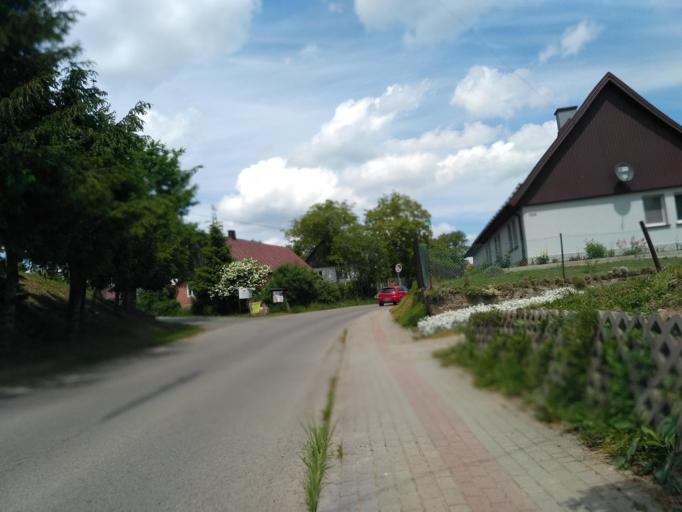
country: PL
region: Subcarpathian Voivodeship
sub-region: Powiat krosnienski
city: Chorkowka
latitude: 49.6117
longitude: 21.6455
